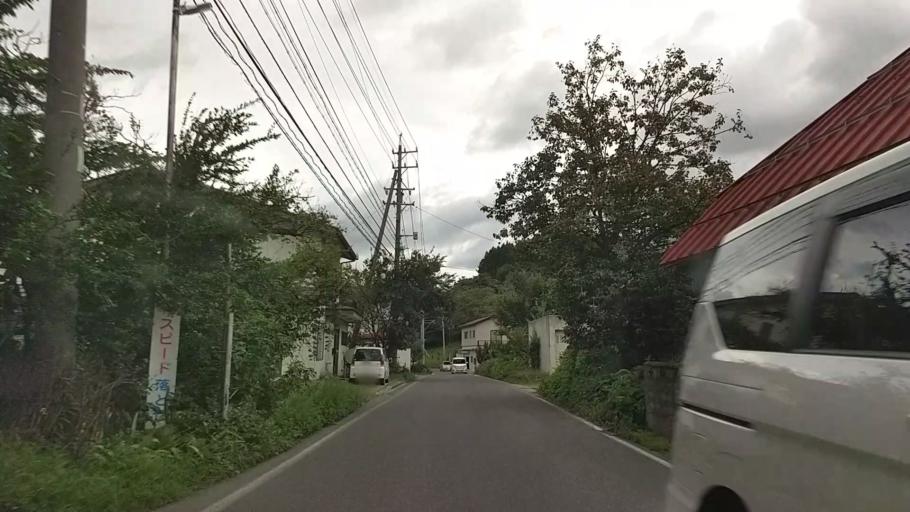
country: JP
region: Nagano
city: Iiyama
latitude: 36.8063
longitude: 138.3601
